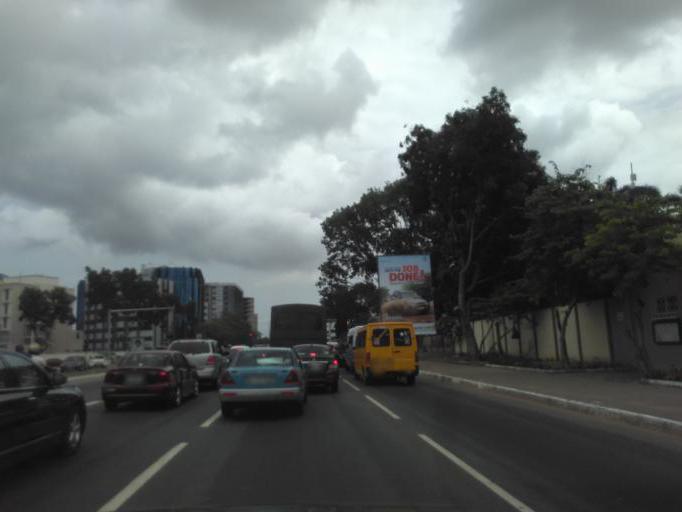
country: GH
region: Greater Accra
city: Accra
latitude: 5.6064
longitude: -0.1775
